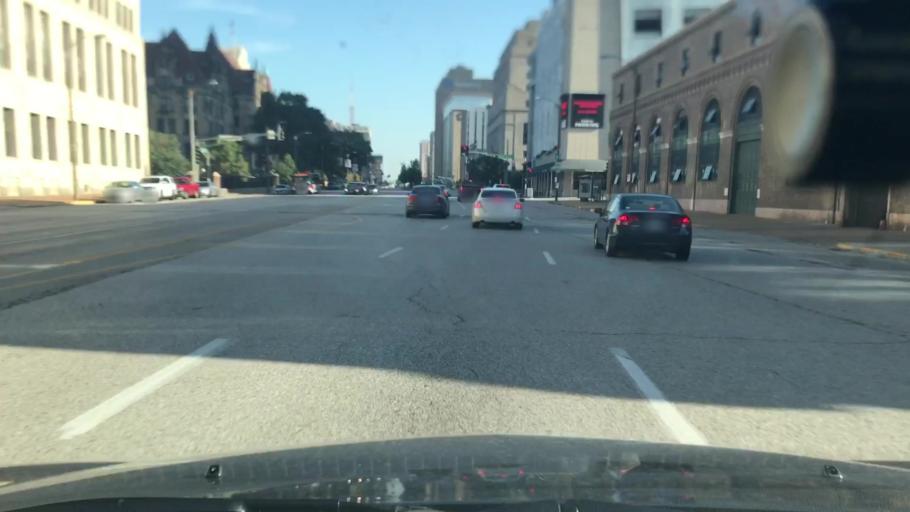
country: US
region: Missouri
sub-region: City of Saint Louis
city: St. Louis
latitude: 38.6244
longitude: -90.1994
